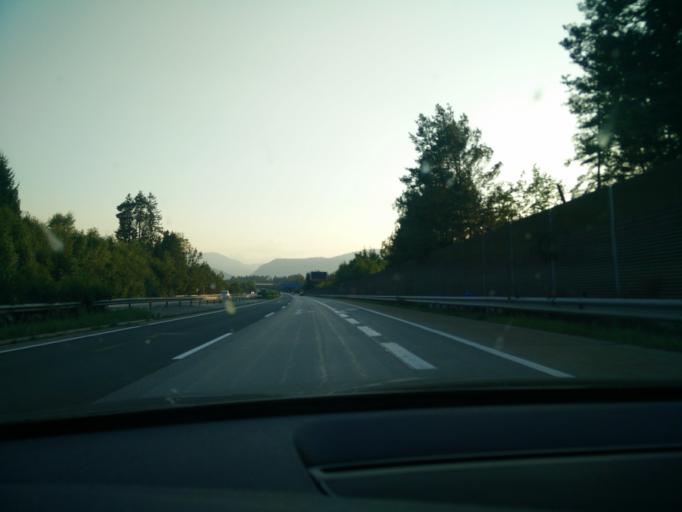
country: AT
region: Carinthia
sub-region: Politischer Bezirk Villach Land
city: Wernberg
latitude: 46.6225
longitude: 13.9146
